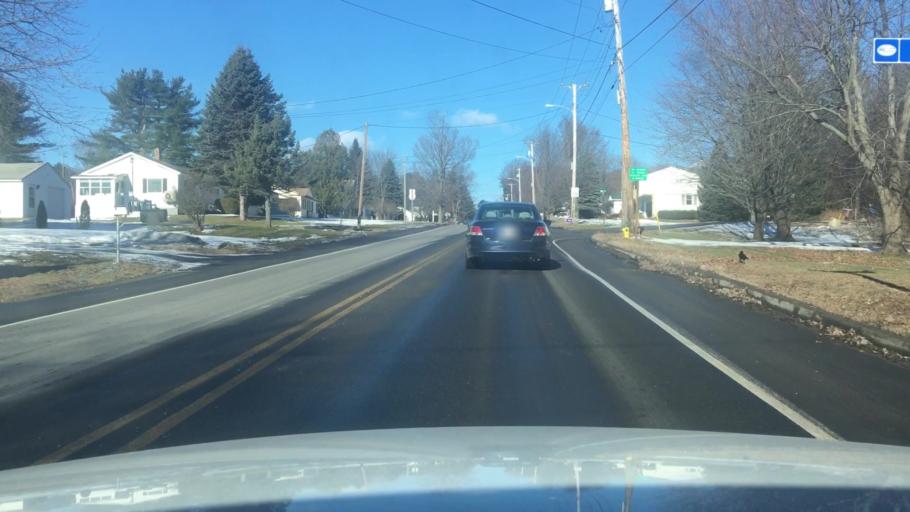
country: US
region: Maine
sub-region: Kennebec County
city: Waterville
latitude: 44.5730
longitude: -69.6416
